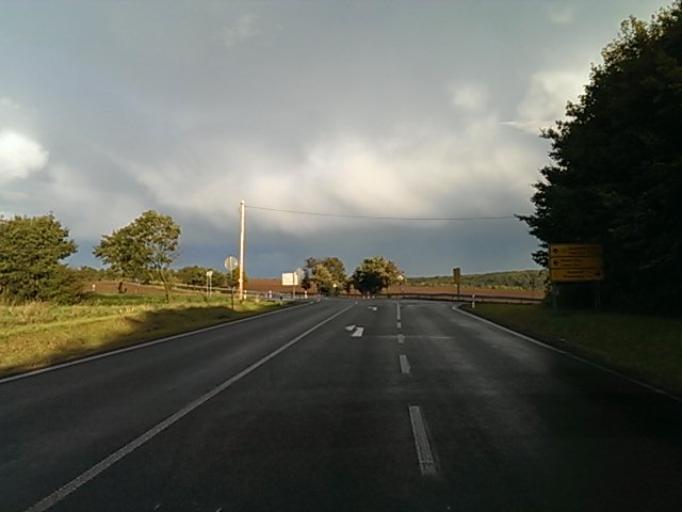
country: DE
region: Thuringia
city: Rastenberg
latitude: 51.1948
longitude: 11.3995
